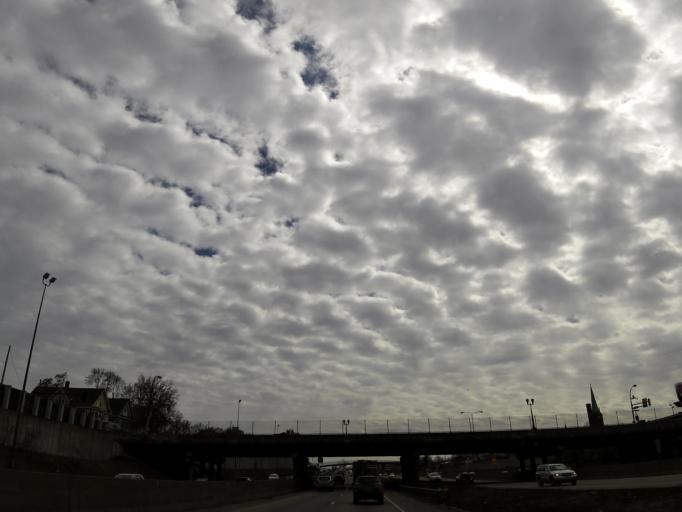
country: US
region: Minnesota
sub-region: Hennepin County
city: Minneapolis
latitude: 44.9635
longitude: -93.2695
